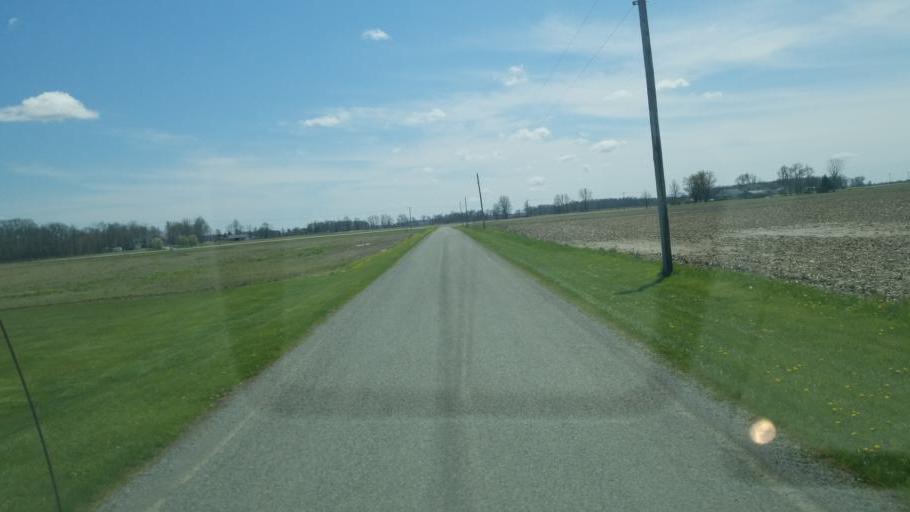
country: US
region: Ohio
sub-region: Union County
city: Richwood
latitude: 40.5025
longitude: -83.2900
